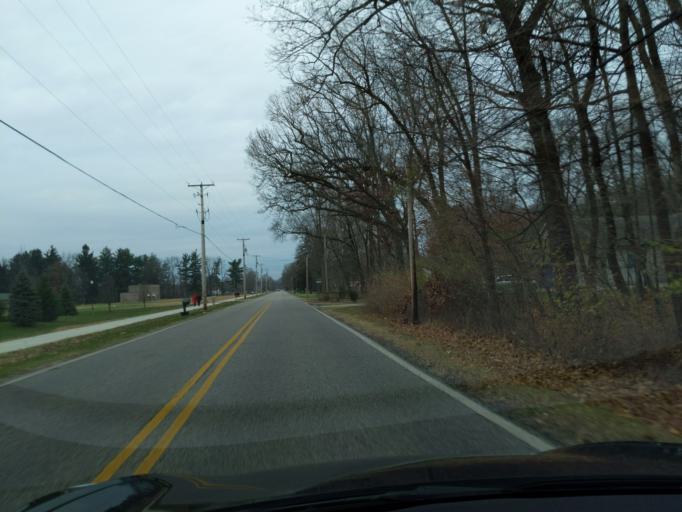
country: US
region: Indiana
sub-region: Saint Joseph County
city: Georgetown
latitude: 41.7323
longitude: -86.2653
